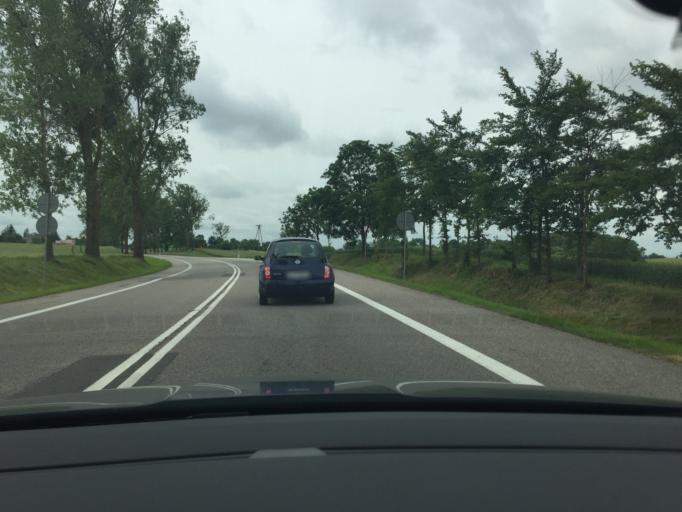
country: PL
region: Pomeranian Voivodeship
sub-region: Powiat tczewski
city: Gniew
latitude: 53.7713
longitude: 18.7696
